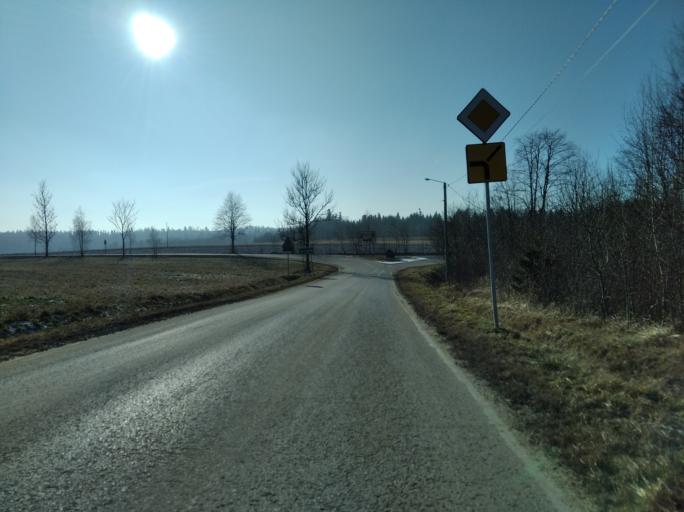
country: PL
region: Subcarpathian Voivodeship
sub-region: Powiat rzeszowski
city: Straszydle
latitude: 49.8784
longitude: 21.9844
